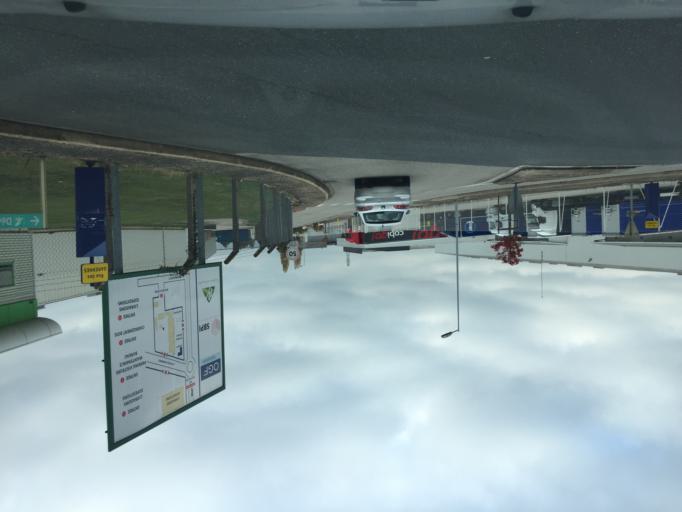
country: FR
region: Rhone-Alpes
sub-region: Departement de l'Ain
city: Reyrieux
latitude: 45.9448
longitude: 4.8141
